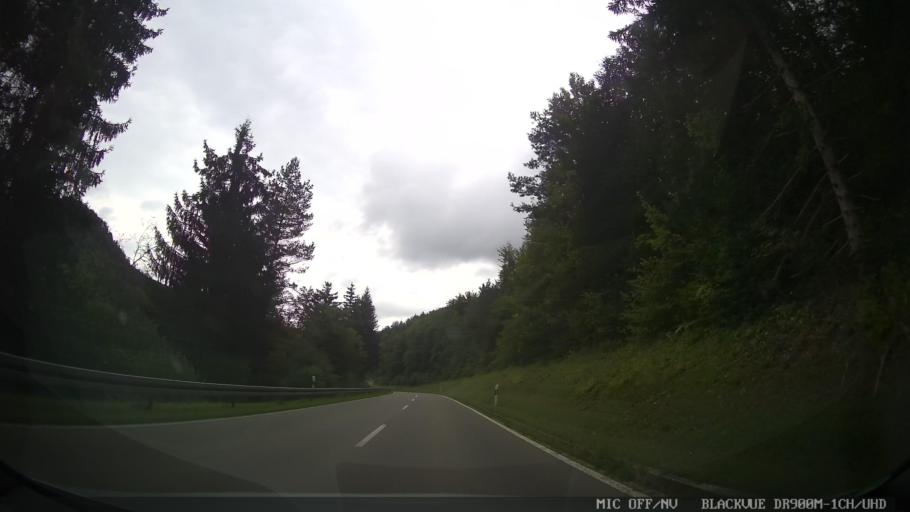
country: DE
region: Baden-Wuerttemberg
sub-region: Freiburg Region
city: Barenthal
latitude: 48.0458
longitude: 8.9291
